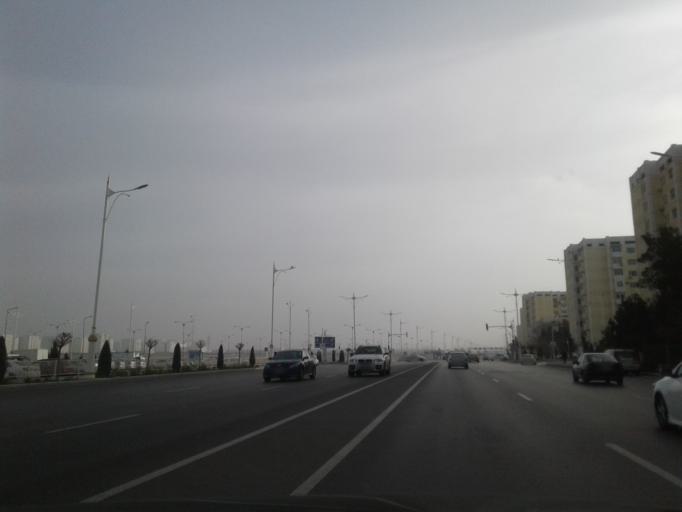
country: TM
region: Ahal
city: Ashgabat
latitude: 37.9000
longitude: 58.3978
